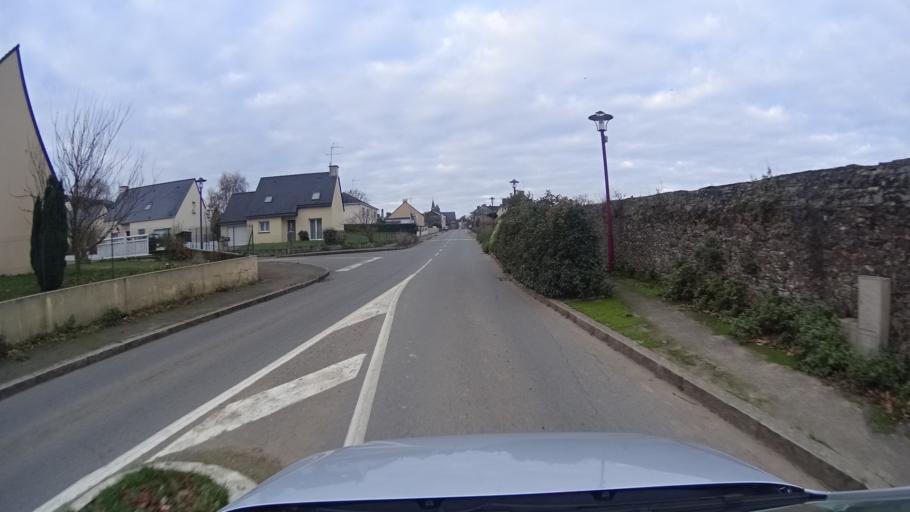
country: FR
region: Pays de la Loire
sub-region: Departement de la Loire-Atlantique
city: Avessac
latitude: 47.6536
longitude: -1.9854
